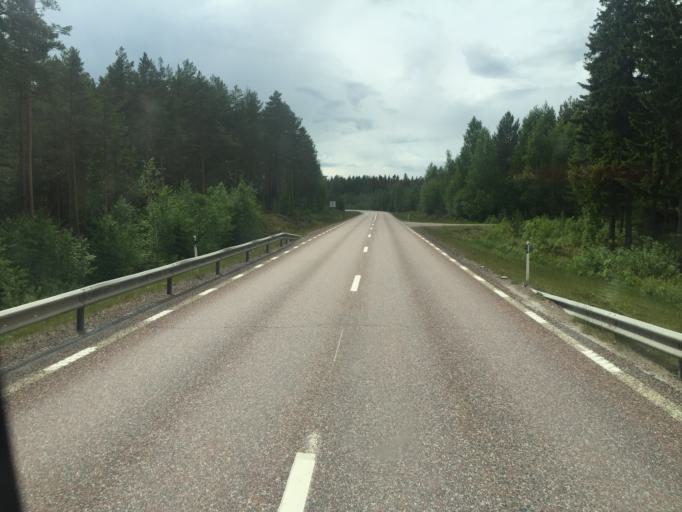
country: SE
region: Dalarna
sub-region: Vansbro Kommun
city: Vansbro
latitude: 60.4940
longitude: 14.1368
